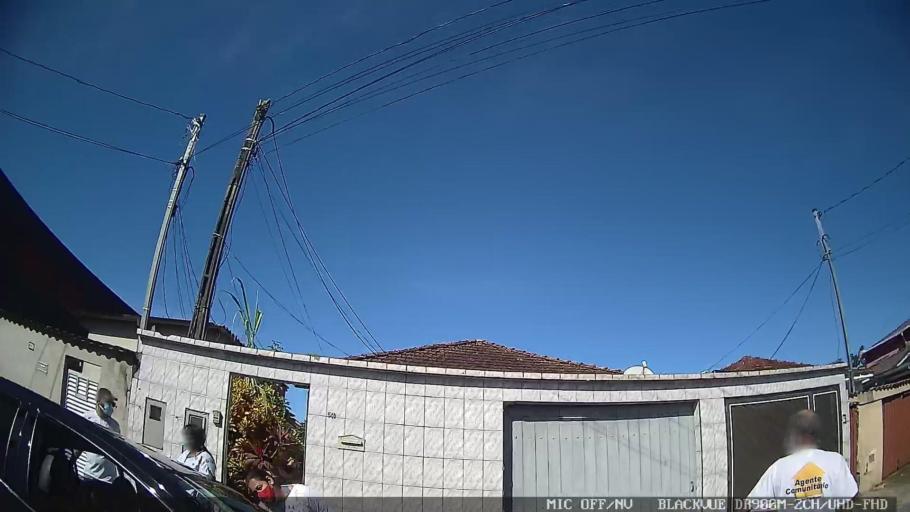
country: BR
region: Sao Paulo
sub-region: Santos
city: Santos
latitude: -23.9387
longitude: -46.2909
